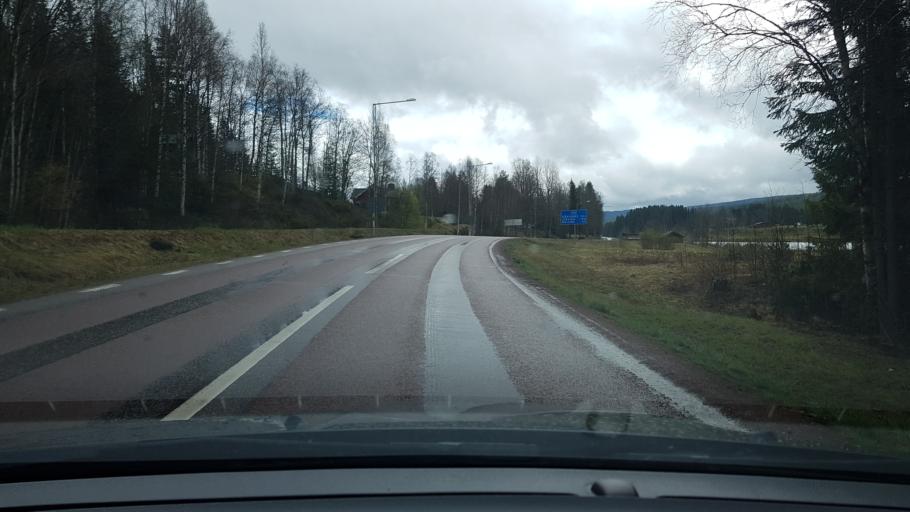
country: SE
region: Dalarna
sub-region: Malung-Saelens kommun
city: Malung
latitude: 61.1477
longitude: 13.2742
